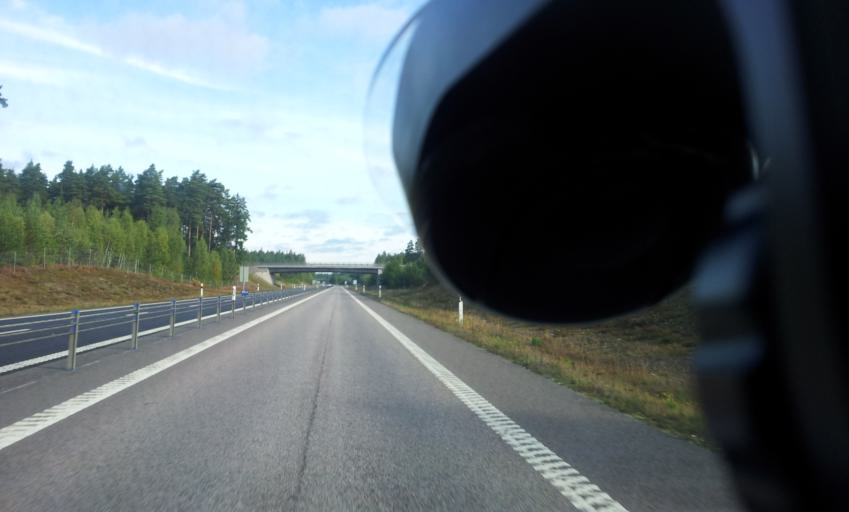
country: SE
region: Kalmar
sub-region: Torsas Kommun
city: Torsas
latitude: 56.4998
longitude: 16.0861
